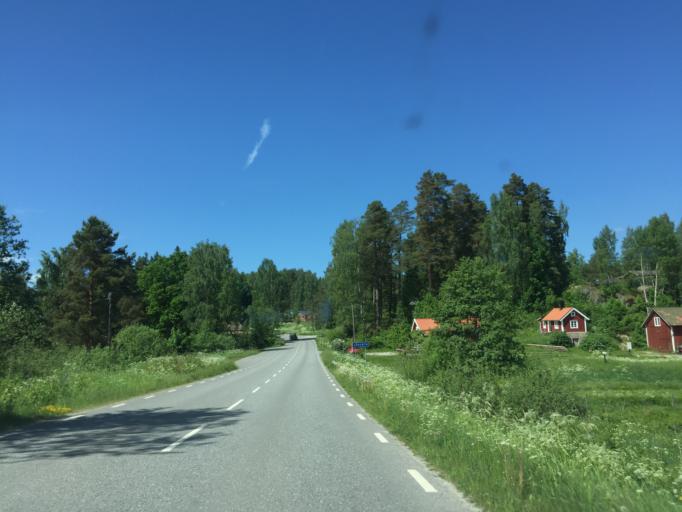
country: SE
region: OErebro
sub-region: Orebro Kommun
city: Hovsta
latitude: 59.3847
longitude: 15.2075
